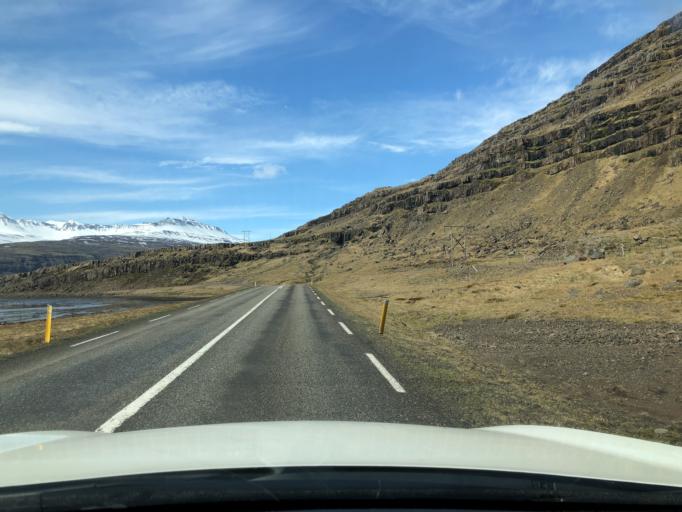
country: IS
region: East
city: Reydarfjoerdur
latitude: 64.6577
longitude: -14.4711
